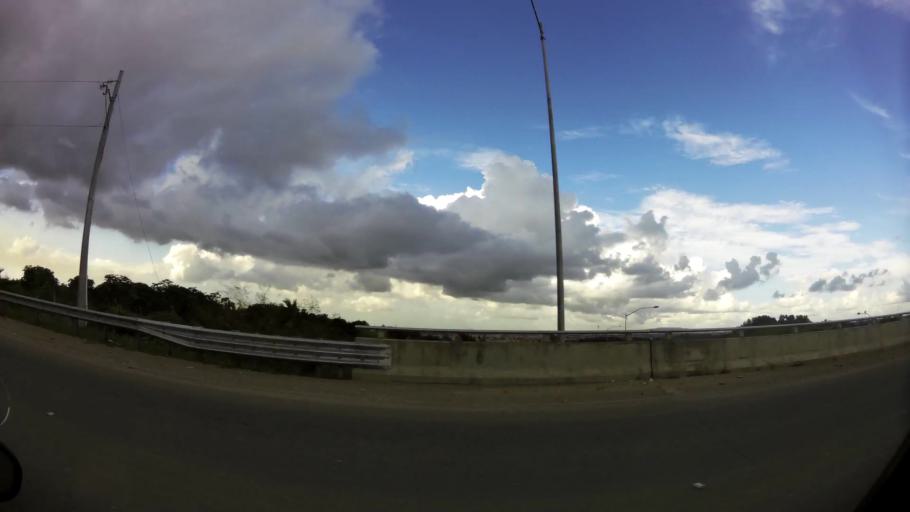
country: TT
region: City of San Fernando
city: Mon Repos
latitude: 10.2448
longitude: -61.4451
